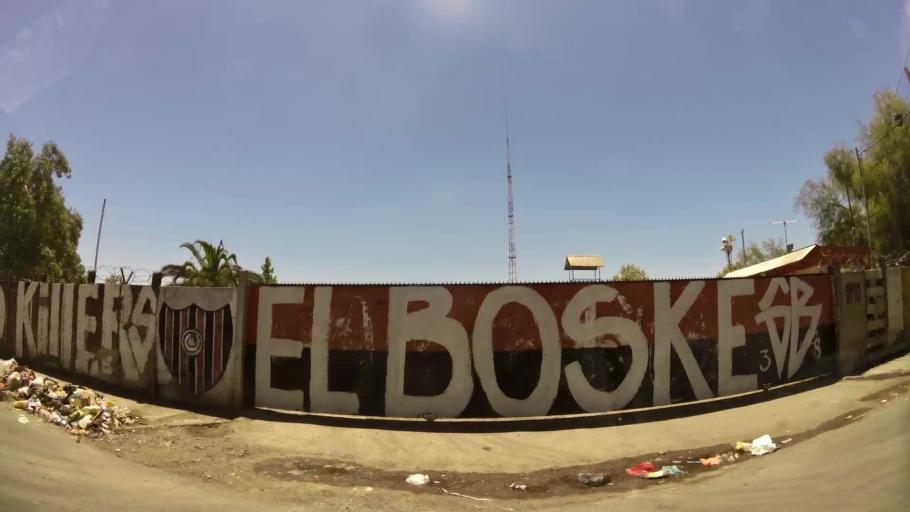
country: CL
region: Santiago Metropolitan
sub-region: Provincia de Maipo
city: San Bernardo
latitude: -33.5808
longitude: -70.6686
